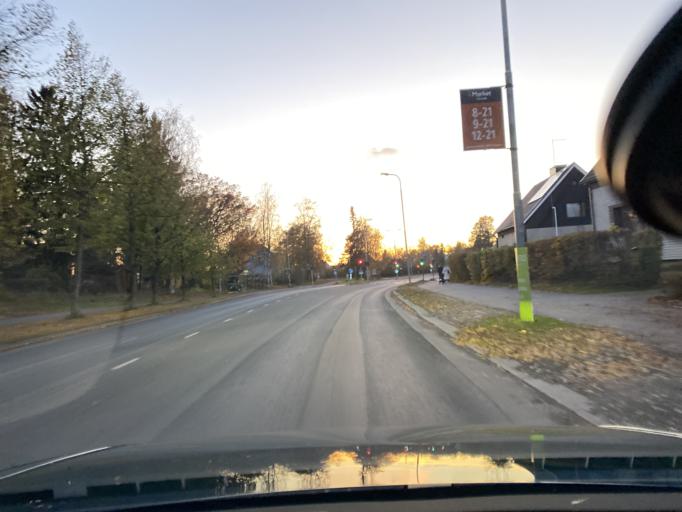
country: FI
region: Pirkanmaa
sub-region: Tampere
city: Tampere
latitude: 61.4703
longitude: 23.7519
